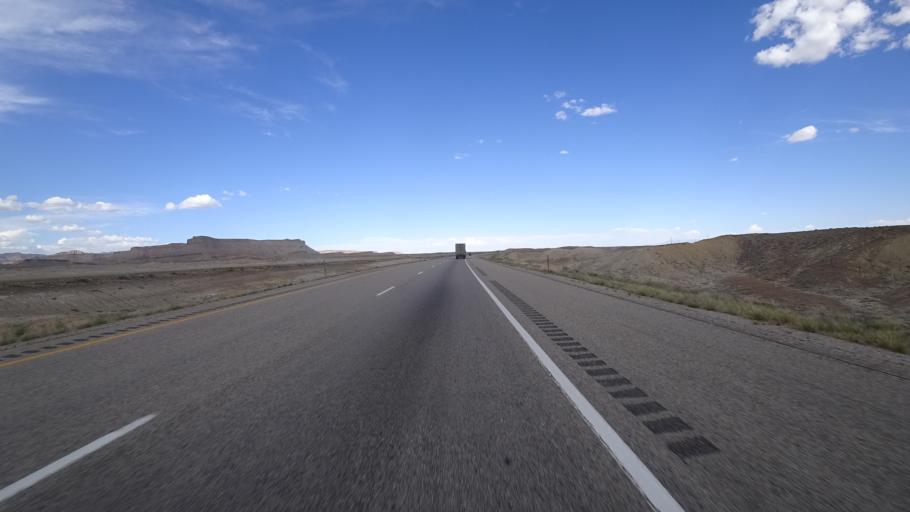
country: US
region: Utah
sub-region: Grand County
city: Moab
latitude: 38.9258
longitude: -109.9925
